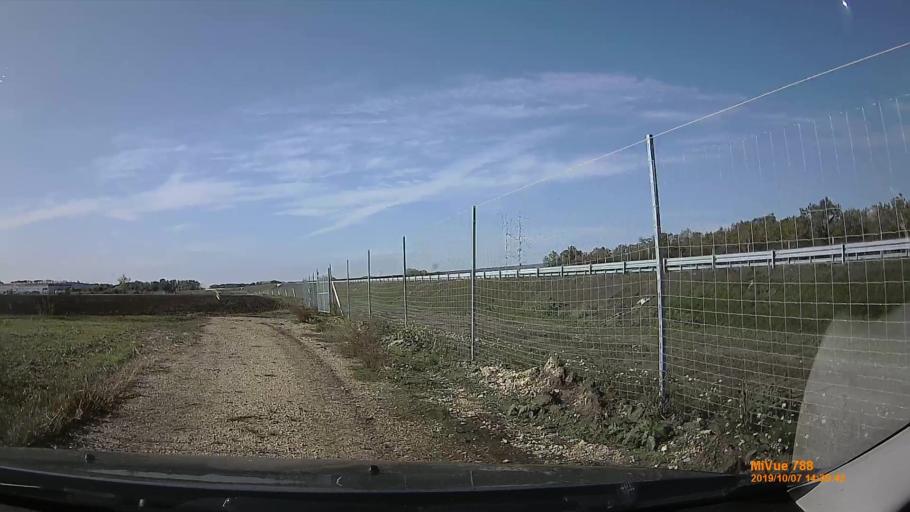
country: HU
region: Jasz-Nagykun-Szolnok
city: Kunszentmarton
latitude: 46.8585
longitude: 20.3058
